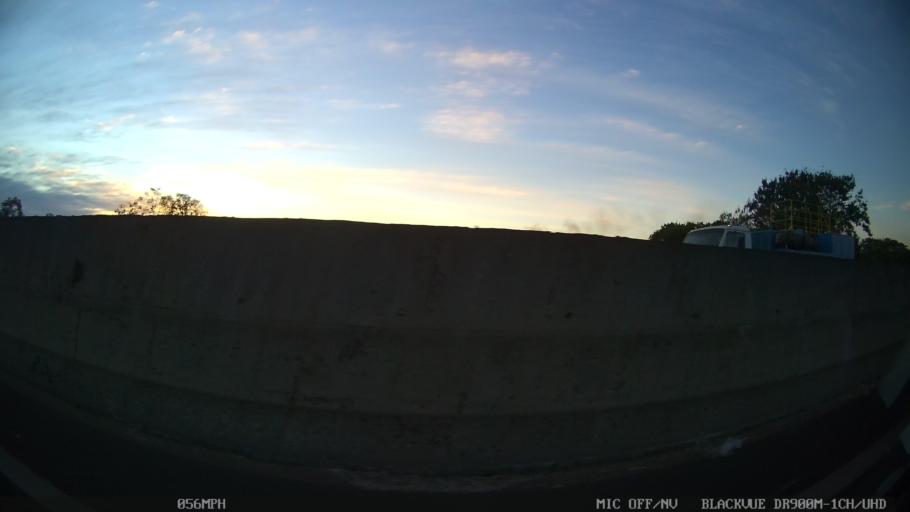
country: BR
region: Sao Paulo
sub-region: Catanduva
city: Catanduva
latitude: -21.1131
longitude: -48.9727
